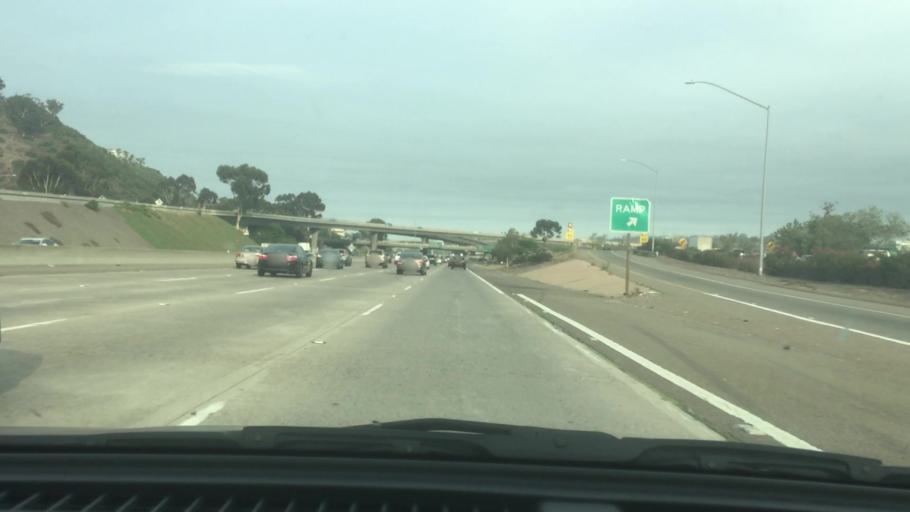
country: US
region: California
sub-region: San Diego County
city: San Diego
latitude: 32.7793
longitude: -117.1072
